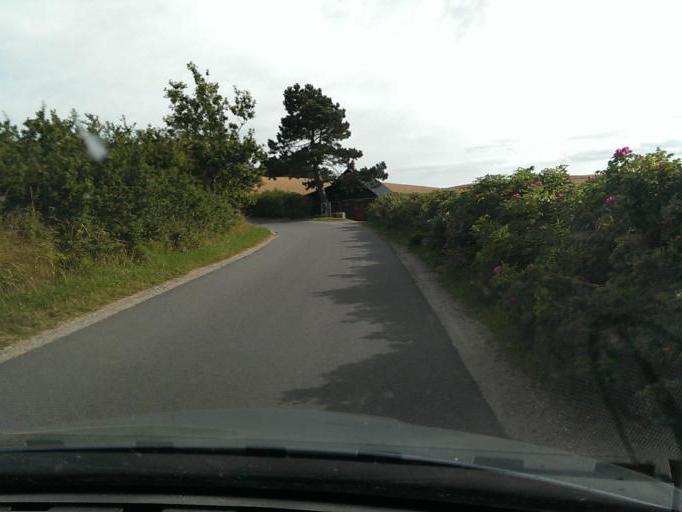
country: DK
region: Central Jutland
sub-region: Syddjurs Kommune
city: Ronde
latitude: 56.1154
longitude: 10.5045
